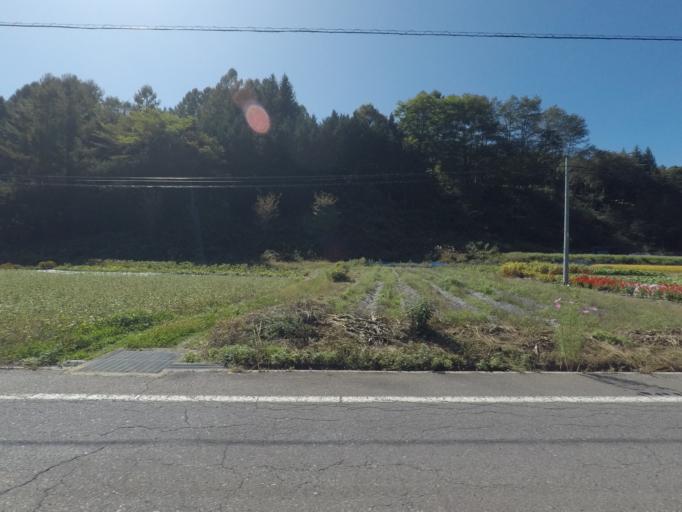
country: JP
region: Nagano
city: Tatsuno
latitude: 35.9732
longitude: 137.7532
